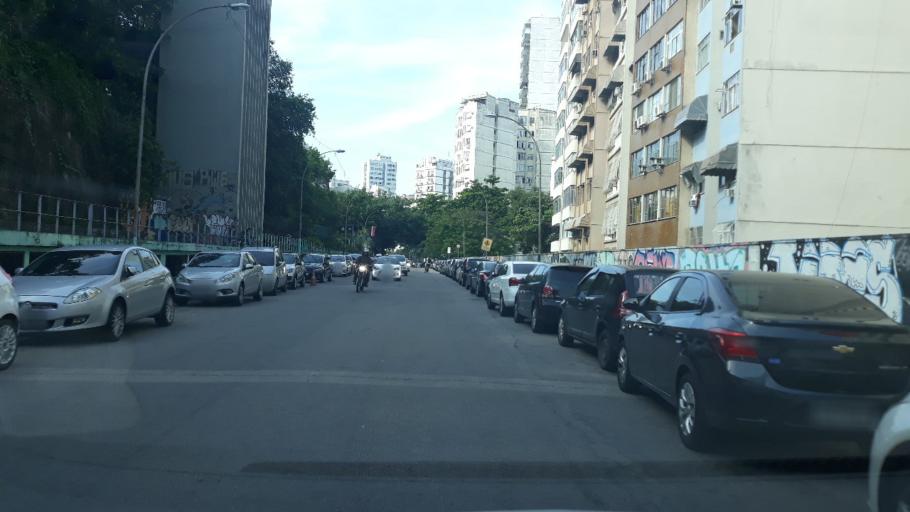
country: BR
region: Rio de Janeiro
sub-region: Rio De Janeiro
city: Rio de Janeiro
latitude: -22.9381
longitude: -43.1787
